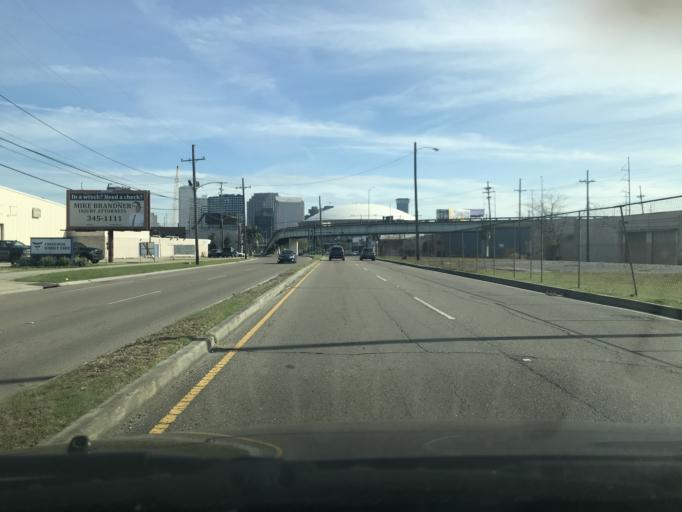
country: US
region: Louisiana
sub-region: Orleans Parish
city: New Orleans
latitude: 29.9567
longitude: -90.0889
